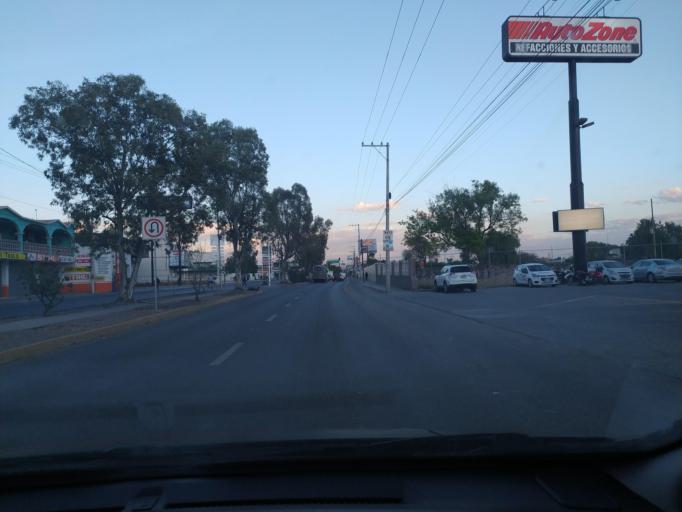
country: LA
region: Oudomxai
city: Muang La
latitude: 21.0287
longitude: 101.8633
